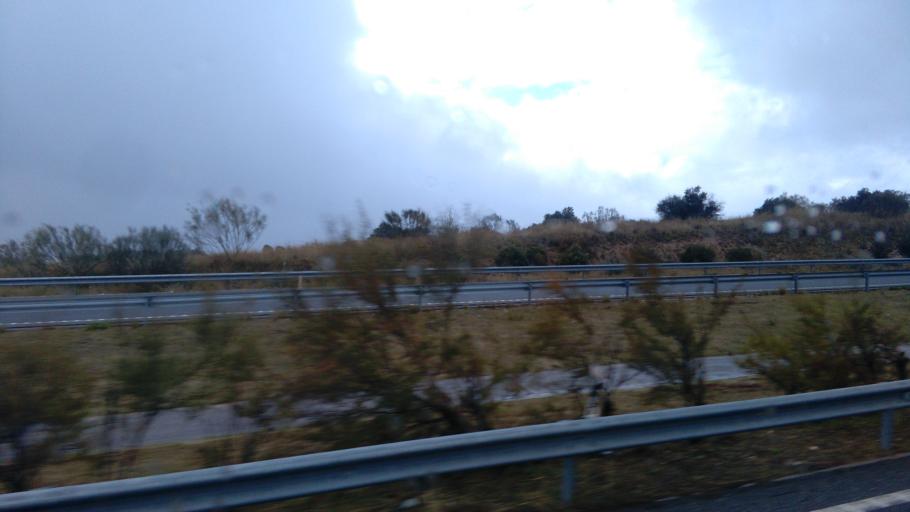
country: ES
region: Madrid
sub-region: Provincia de Madrid
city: Arroyomolinos
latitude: 40.2607
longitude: -3.9586
